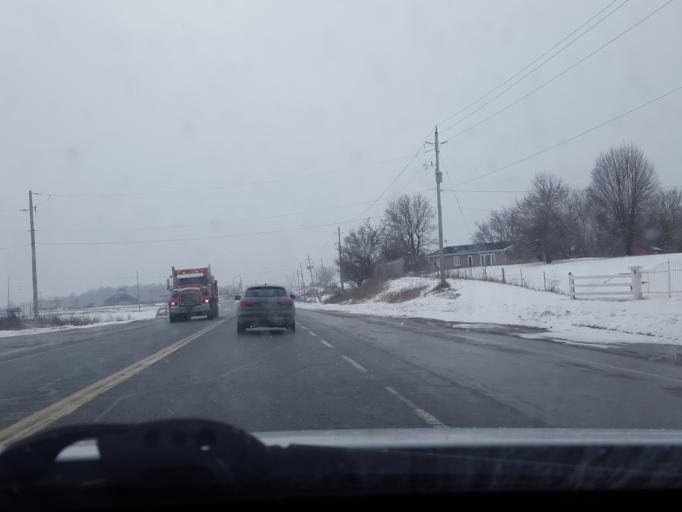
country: CA
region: Ontario
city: Markham
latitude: 44.0021
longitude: -79.2841
